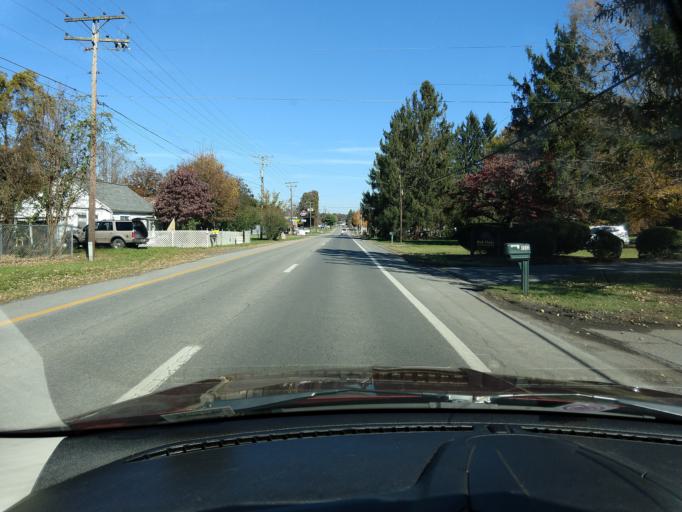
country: US
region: West Virginia
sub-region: Greenbrier County
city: Fairlea
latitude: 37.7742
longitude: -80.4612
